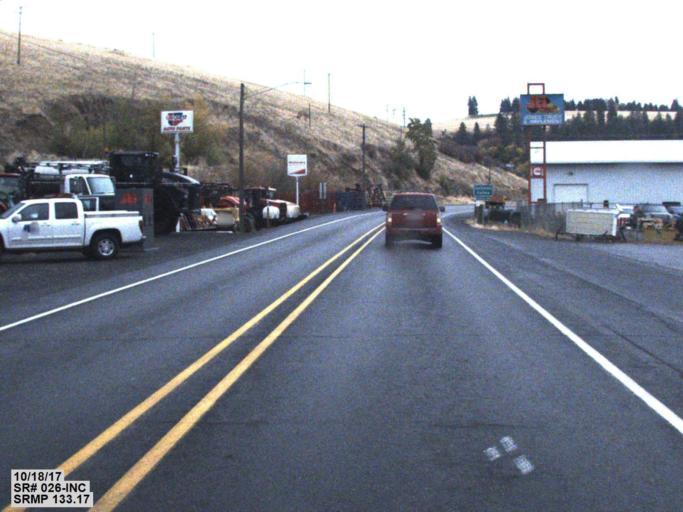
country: US
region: Washington
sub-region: Whitman County
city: Colfax
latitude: 46.8910
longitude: -117.3707
